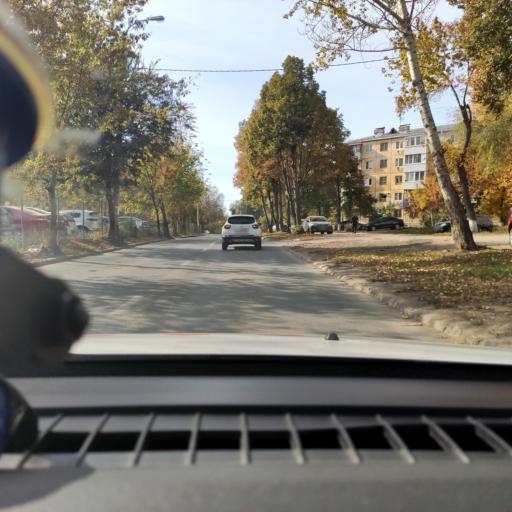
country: RU
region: Samara
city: Samara
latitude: 53.2264
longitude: 50.2138
